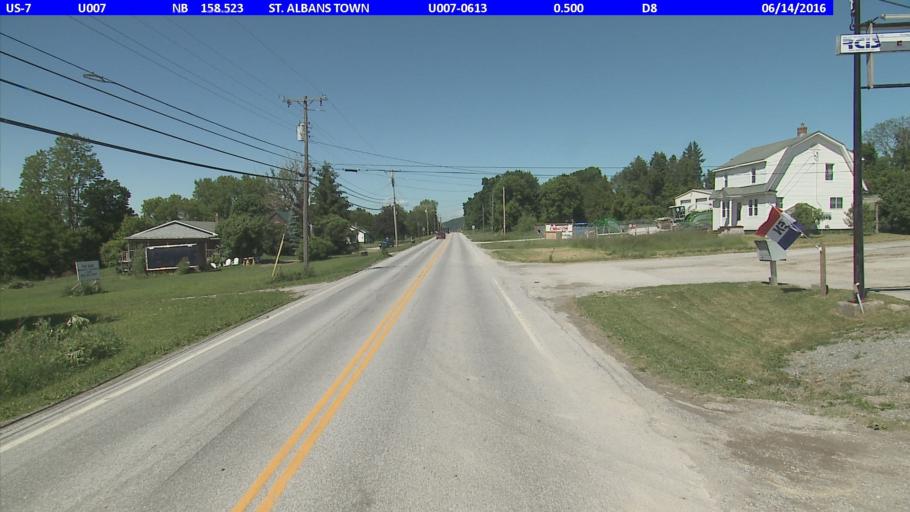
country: US
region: Vermont
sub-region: Franklin County
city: Saint Albans
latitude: 44.7867
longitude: -73.1007
